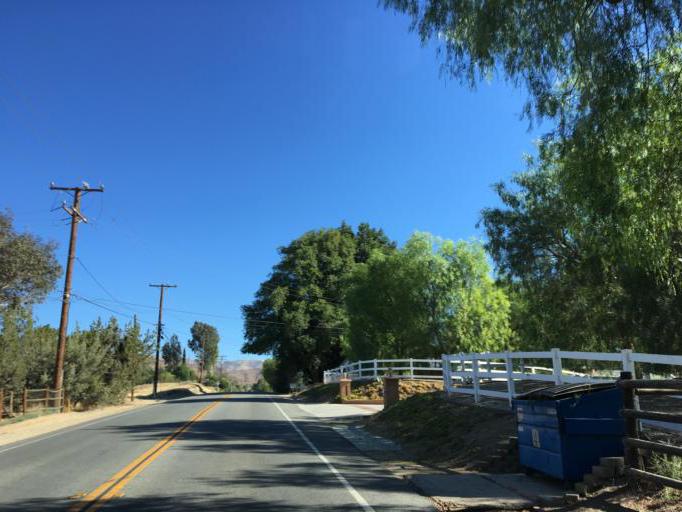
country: US
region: California
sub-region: Los Angeles County
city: Agua Dulce
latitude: 34.4913
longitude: -118.3263
